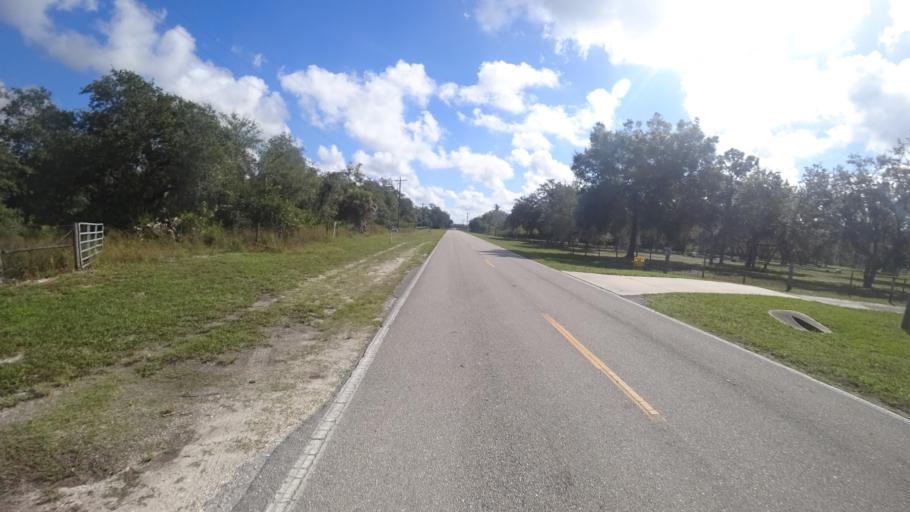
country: US
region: Florida
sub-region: Sarasota County
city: Lake Sarasota
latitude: 27.3392
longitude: -82.1887
